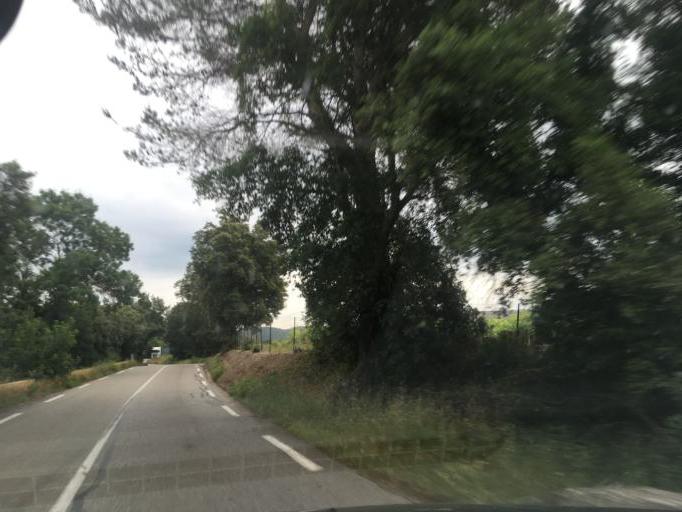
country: FR
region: Provence-Alpes-Cote d'Azur
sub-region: Departement du Var
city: Pierrefeu-du-Var
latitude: 43.2331
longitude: 6.1930
